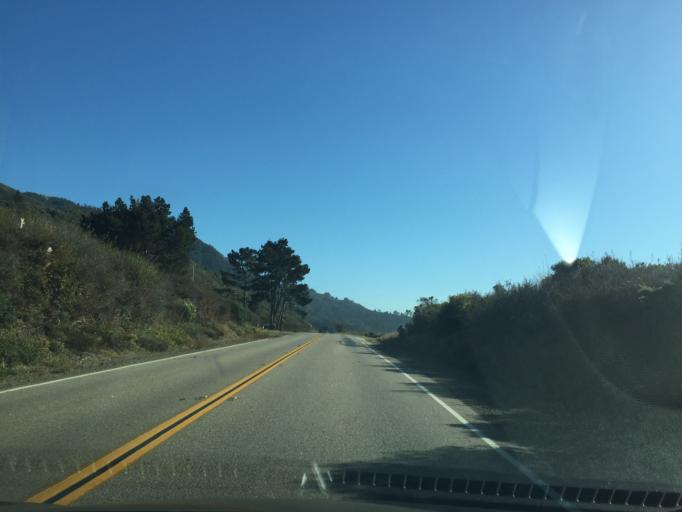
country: US
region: California
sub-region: Monterey County
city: King City
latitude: 35.9334
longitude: -121.4691
